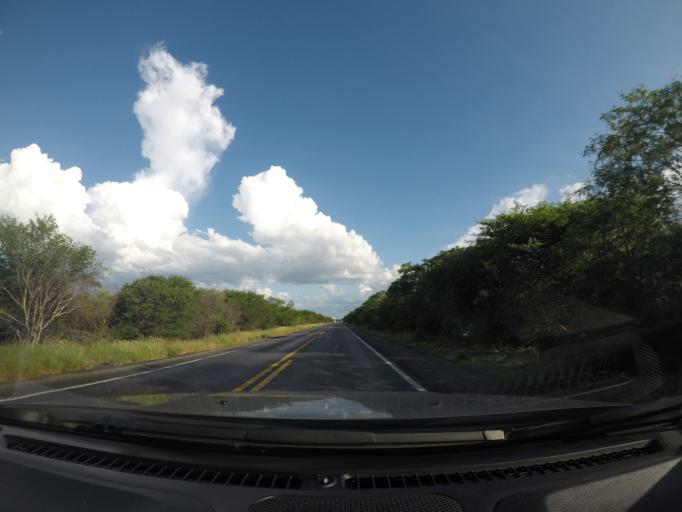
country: BR
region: Bahia
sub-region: Oliveira Dos Brejinhos
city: Oliveira dos Brejinhos
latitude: -12.0936
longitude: -42.9268
